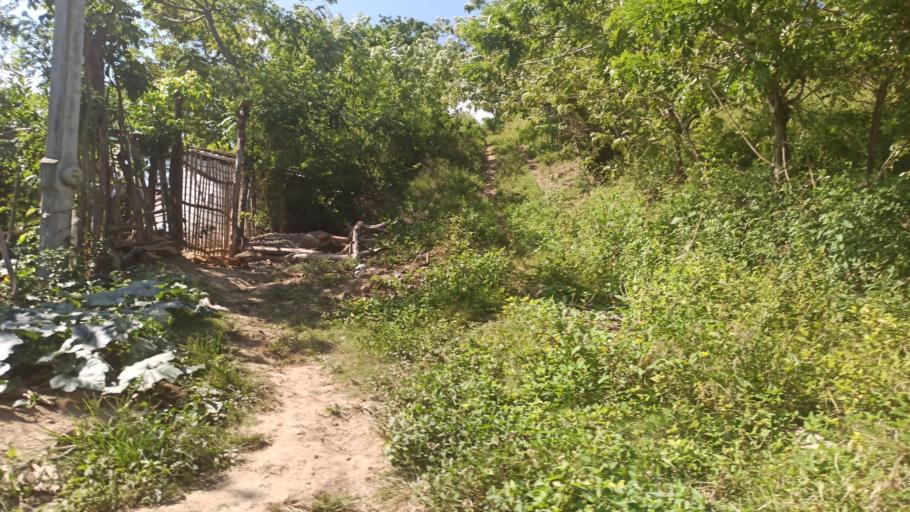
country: MX
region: Veracruz
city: Cazones de Herrera
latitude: 20.6409
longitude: -97.3102
